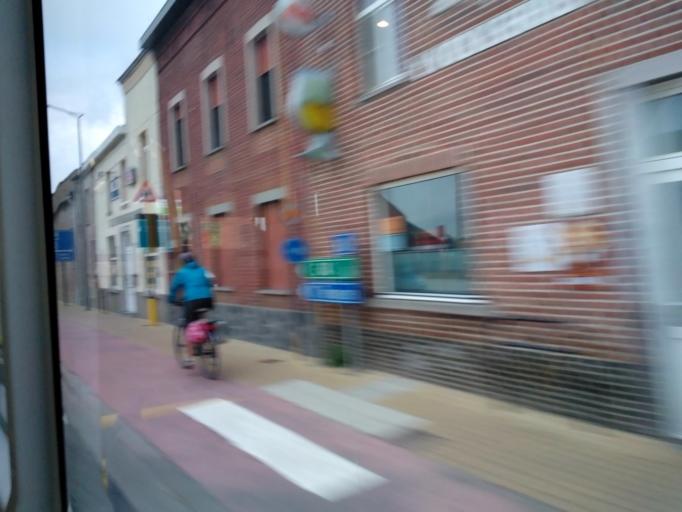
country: BE
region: Flanders
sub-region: Provincie Vlaams-Brabant
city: Bertem
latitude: 50.8662
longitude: 4.6321
